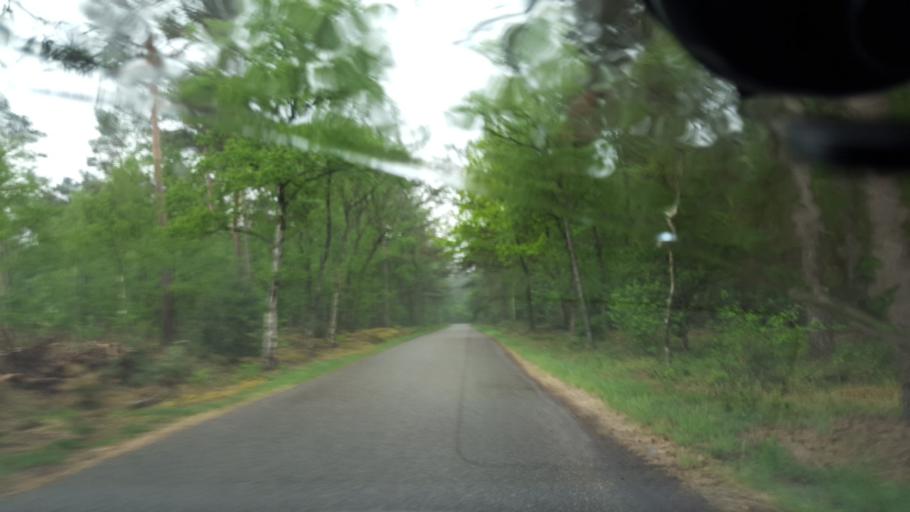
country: NL
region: North Brabant
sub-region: Gemeente Someren
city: Someren
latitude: 51.4041
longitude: 5.6676
